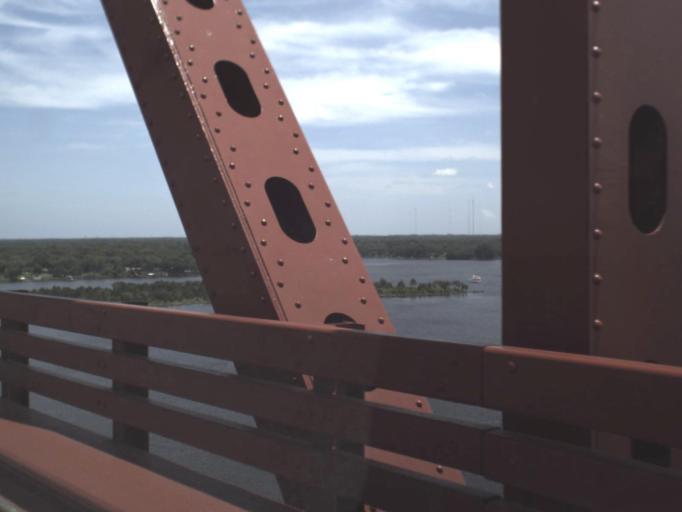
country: US
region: Florida
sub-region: Duval County
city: Jacksonville
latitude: 30.3272
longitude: -81.6240
